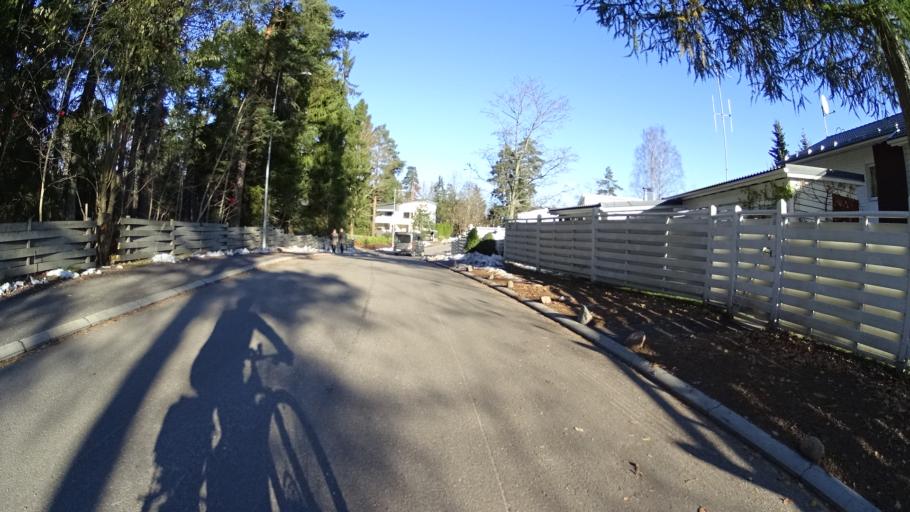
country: FI
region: Uusimaa
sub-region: Helsinki
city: Kilo
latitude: 60.2363
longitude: 24.7529
